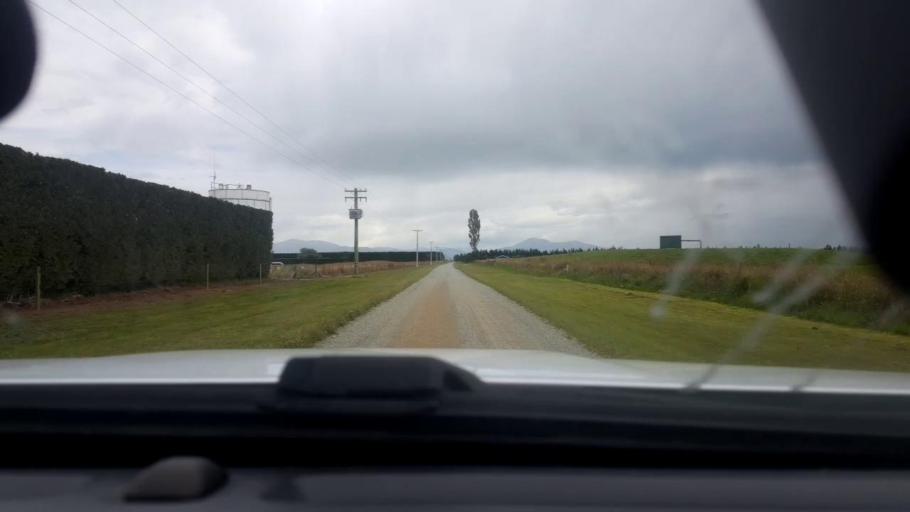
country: NZ
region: Canterbury
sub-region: Timaru District
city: Timaru
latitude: -44.1706
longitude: 171.4149
